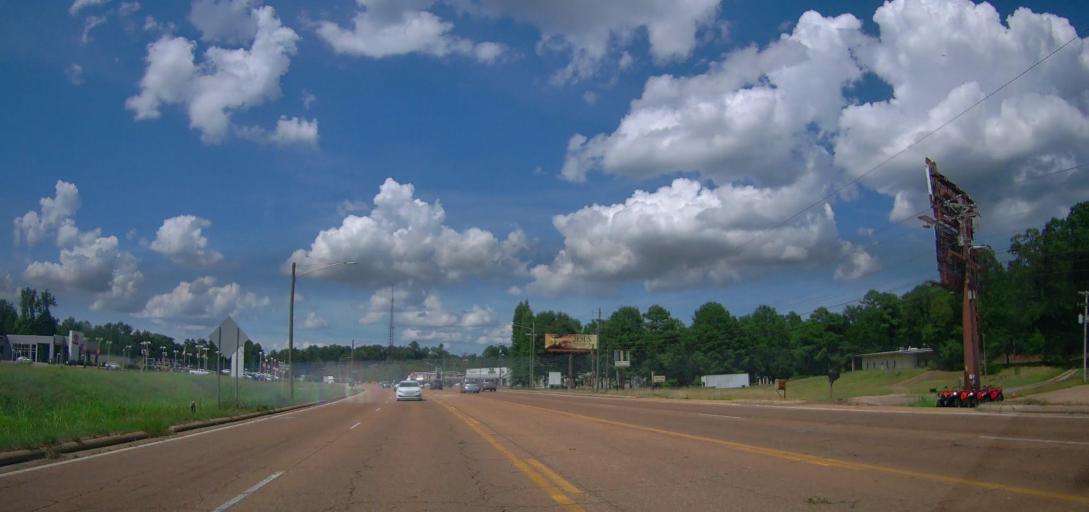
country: US
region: Mississippi
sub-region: Lowndes County
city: Columbus
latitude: 33.5476
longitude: -88.4340
